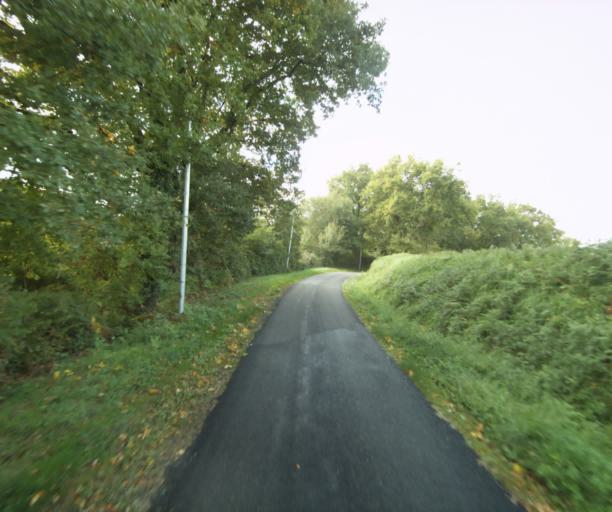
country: FR
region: Midi-Pyrenees
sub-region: Departement du Gers
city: Eauze
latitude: 43.8760
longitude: 0.1089
